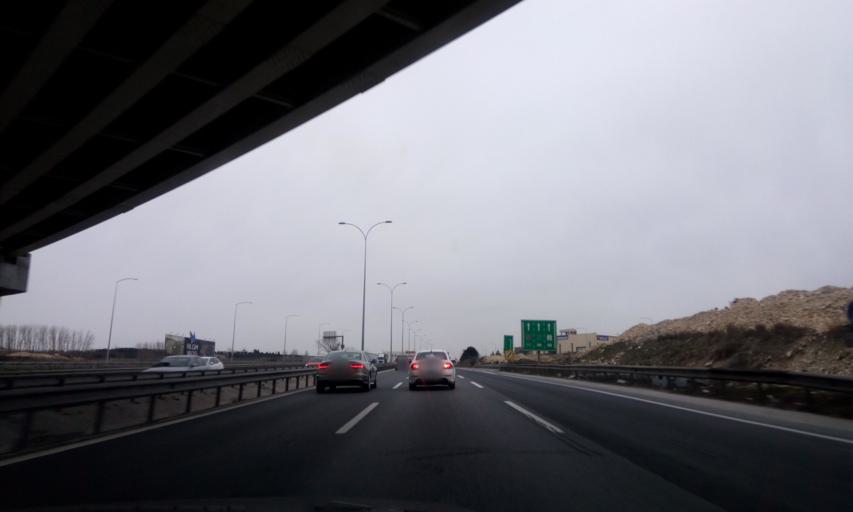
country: TR
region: Kocaeli
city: Tavsanli
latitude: 40.7998
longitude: 29.5075
